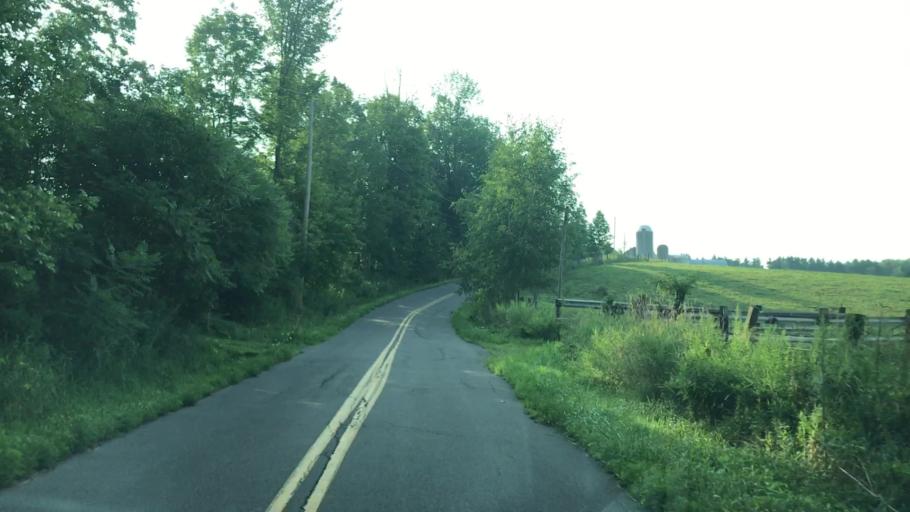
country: US
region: Pennsylvania
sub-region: Wyoming County
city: Factoryville
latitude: 41.6096
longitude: -75.7349
